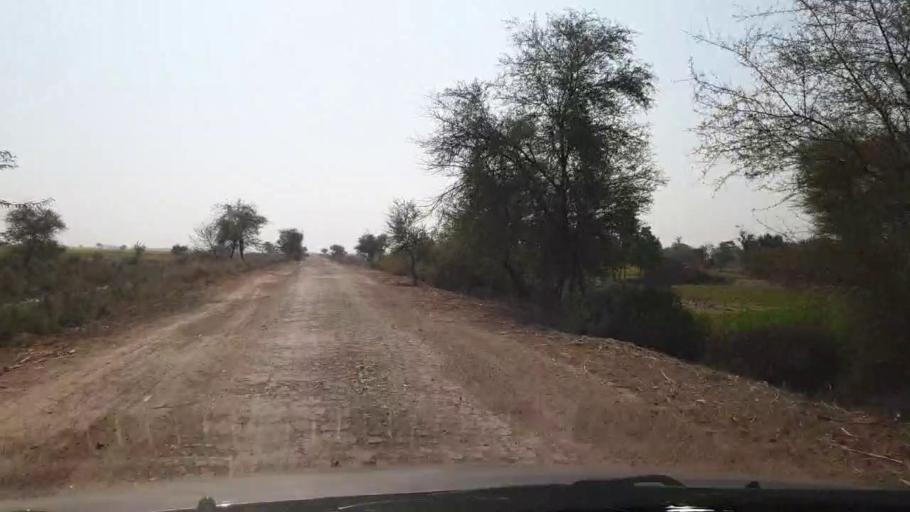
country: PK
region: Sindh
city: Jhol
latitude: 25.8804
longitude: 68.9973
